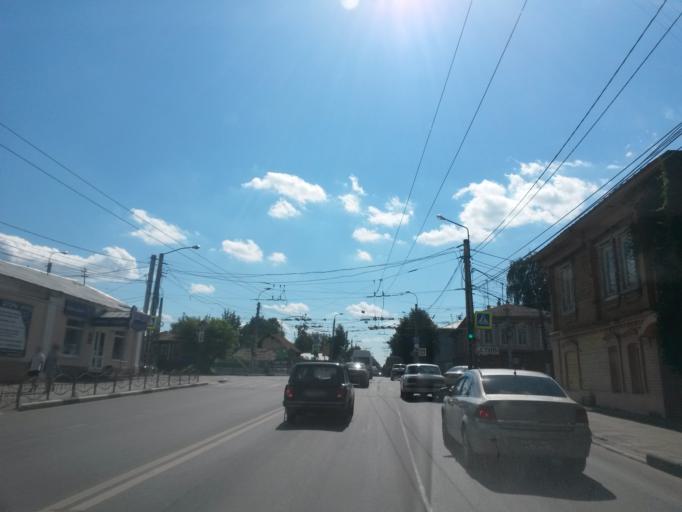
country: RU
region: Ivanovo
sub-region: Gorod Ivanovo
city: Ivanovo
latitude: 56.9931
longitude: 40.9865
